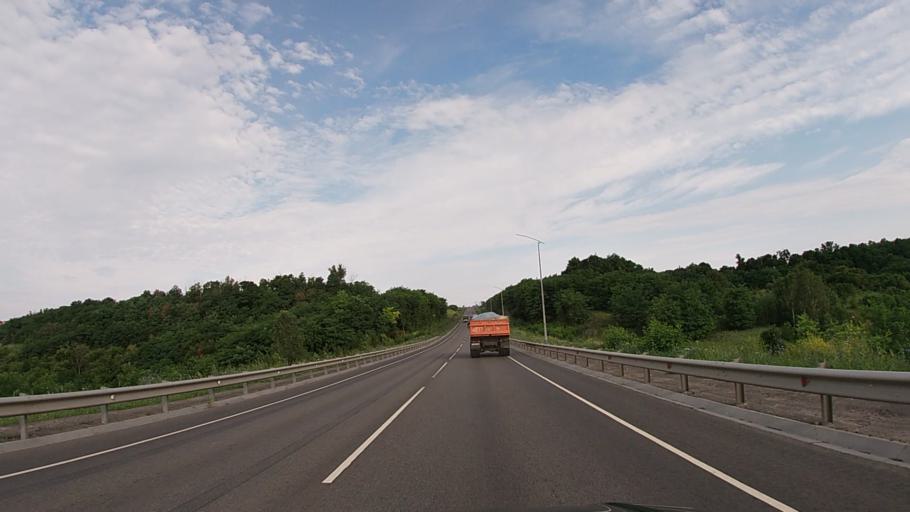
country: RU
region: Belgorod
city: Severnyy
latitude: 50.6681
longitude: 36.4910
